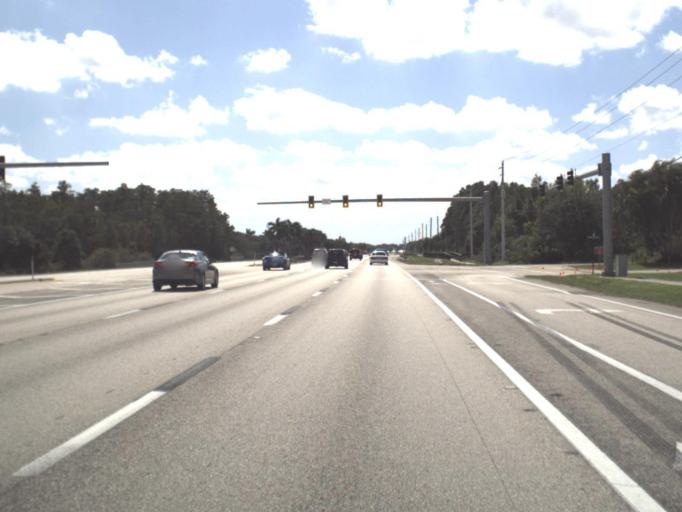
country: US
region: Florida
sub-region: Lee County
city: Estero
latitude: 26.4119
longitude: -81.8121
